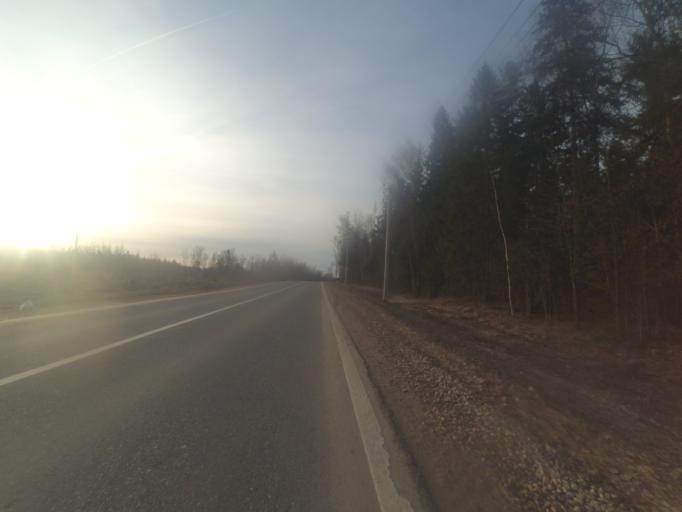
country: RU
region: Moskovskaya
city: Karinskoye
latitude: 55.7686
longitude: 36.6943
